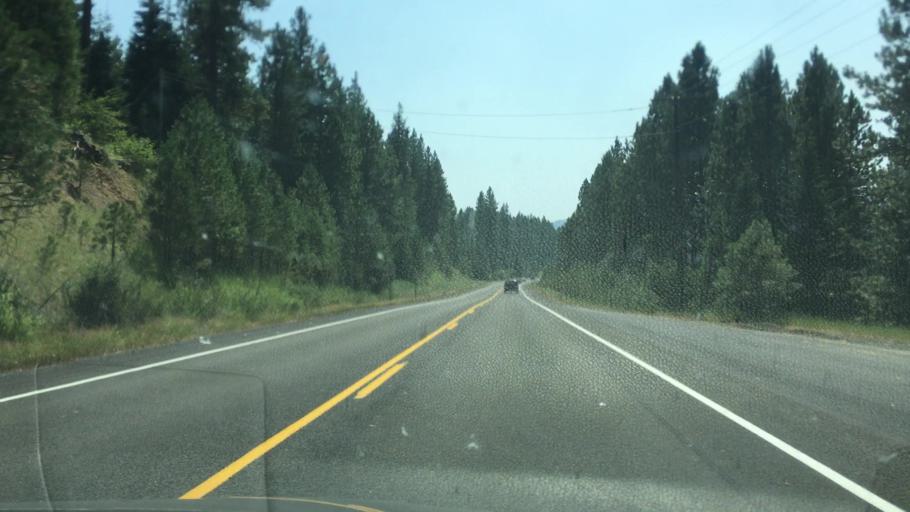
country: US
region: Idaho
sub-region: Valley County
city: McCall
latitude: 45.1097
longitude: -116.3020
